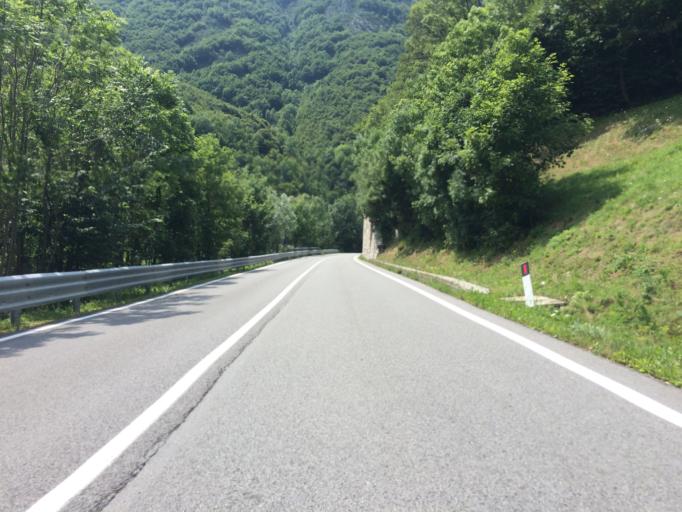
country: IT
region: Piedmont
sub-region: Provincia di Cuneo
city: Vernante
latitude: 44.2285
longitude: 7.5602
